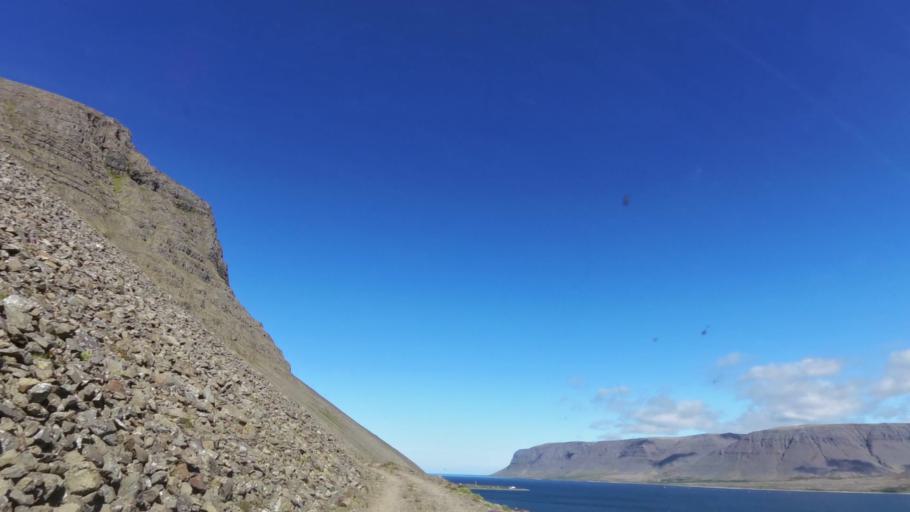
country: IS
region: West
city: Olafsvik
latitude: 65.6288
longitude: -23.9076
